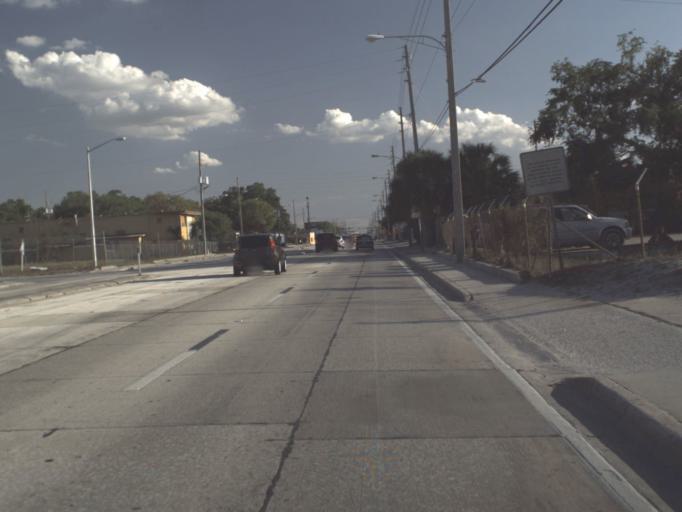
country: US
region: Florida
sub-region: Orange County
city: Orlando
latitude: 28.5252
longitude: -81.3972
